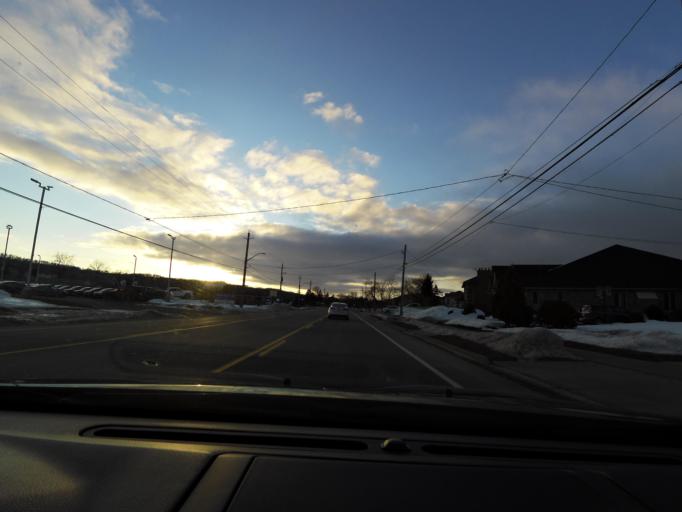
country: CA
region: Ontario
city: Hamilton
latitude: 43.2060
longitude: -79.6270
